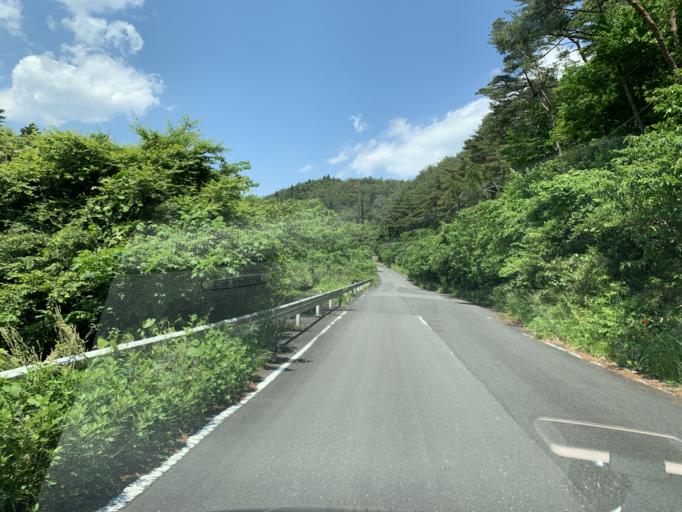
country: JP
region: Miyagi
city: Matsushima
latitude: 38.3544
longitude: 141.0575
